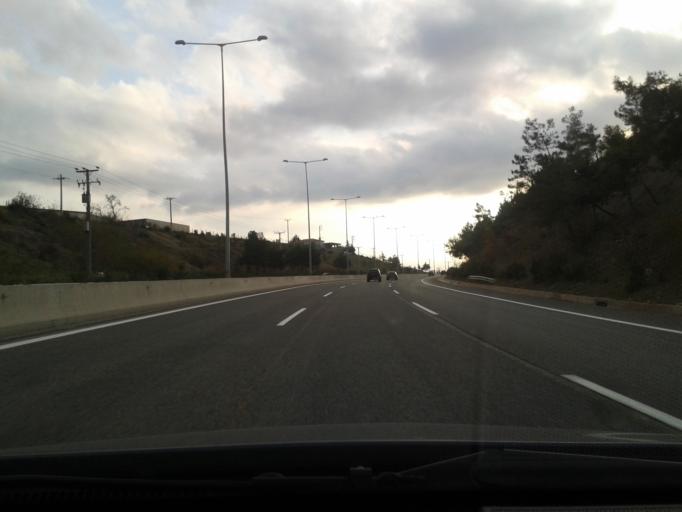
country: GR
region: Attica
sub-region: Nomarchia Anatolikis Attikis
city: Agios Stefanos
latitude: 38.1532
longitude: 23.8549
